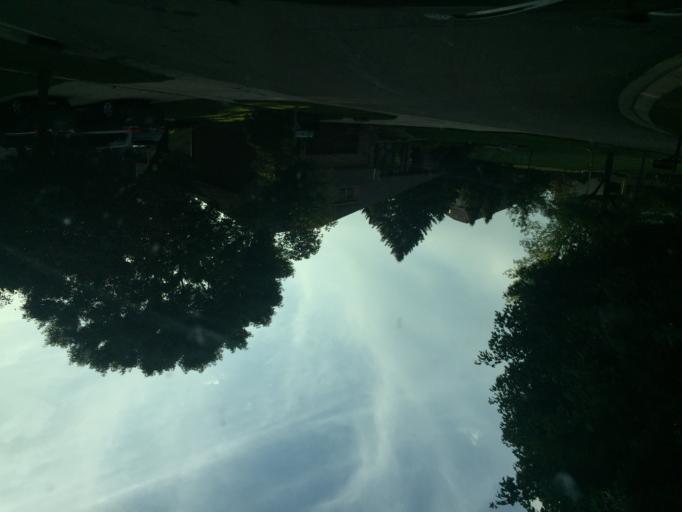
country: US
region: Minnesota
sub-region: Olmsted County
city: Rochester
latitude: 44.0167
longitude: -92.4942
